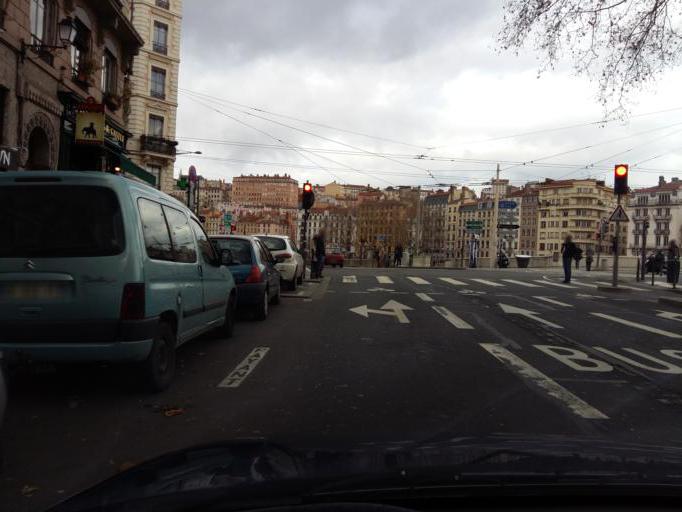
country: FR
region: Rhone-Alpes
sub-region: Departement du Rhone
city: Lyon
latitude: 45.7659
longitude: 4.8289
